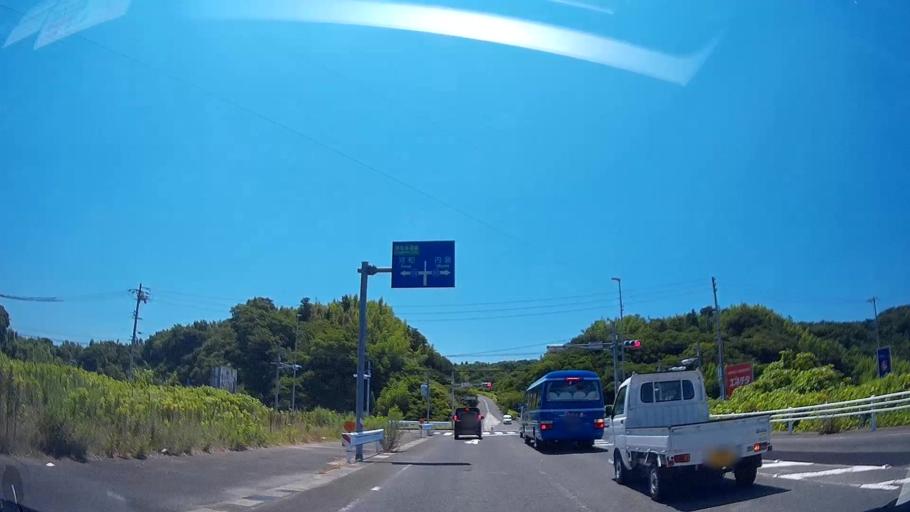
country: JP
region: Aichi
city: Toyohama
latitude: 34.7562
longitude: 136.8860
